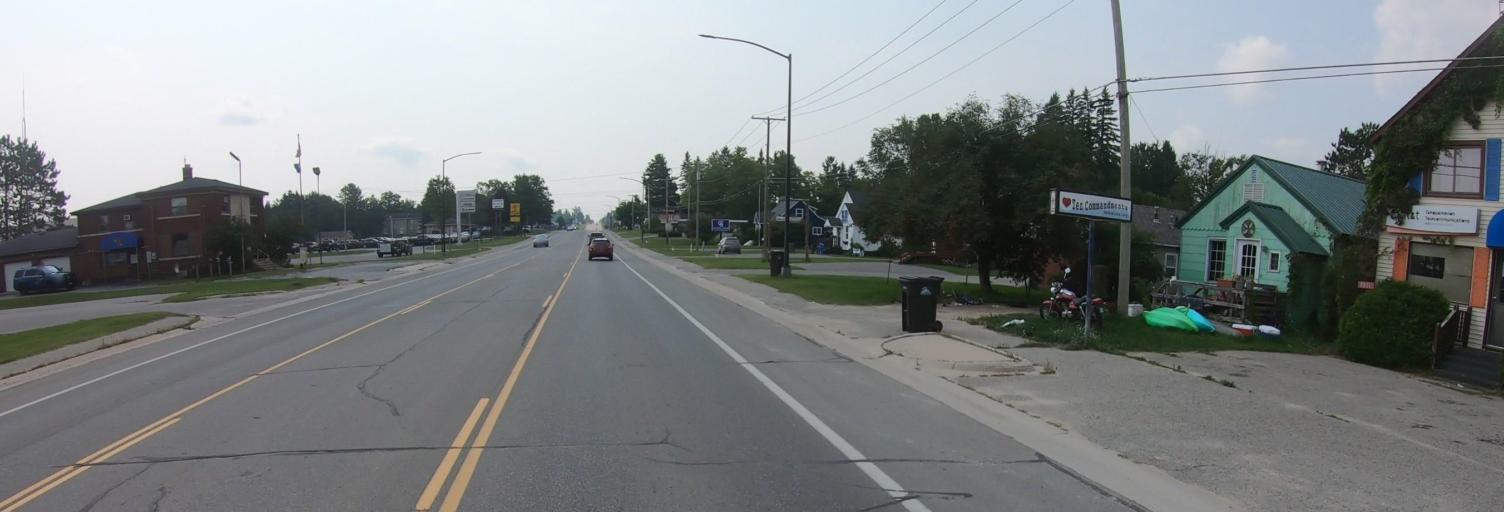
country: US
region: Michigan
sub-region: Luce County
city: Newberry
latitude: 46.3462
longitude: -85.5099
